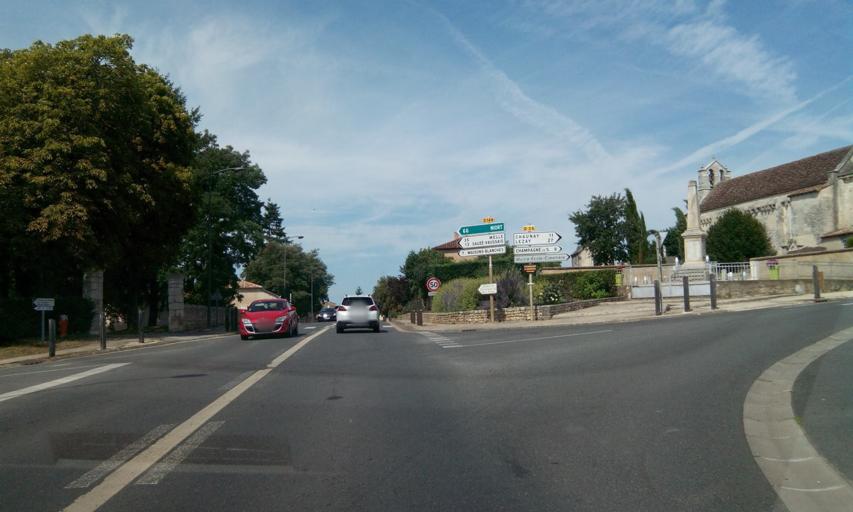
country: FR
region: Poitou-Charentes
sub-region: Departement de la Vienne
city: Civray
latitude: 46.1502
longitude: 0.2707
